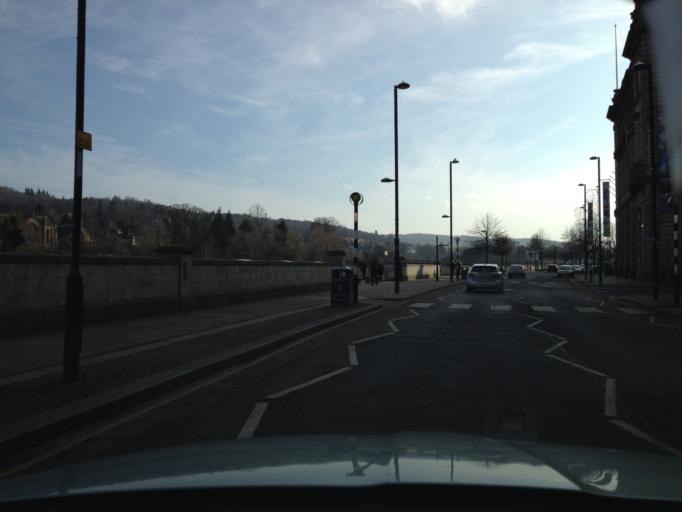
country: GB
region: Scotland
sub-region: Perth and Kinross
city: Perth
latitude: 56.3974
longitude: -3.4260
